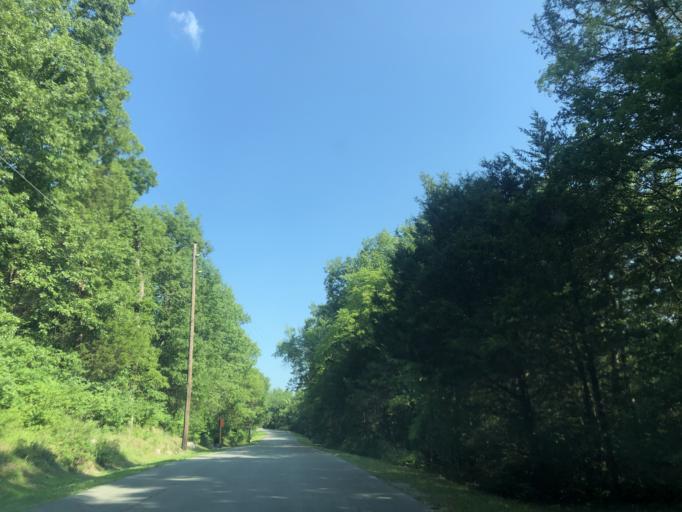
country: US
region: Tennessee
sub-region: Wilson County
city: Green Hill
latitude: 36.1367
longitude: -86.5959
